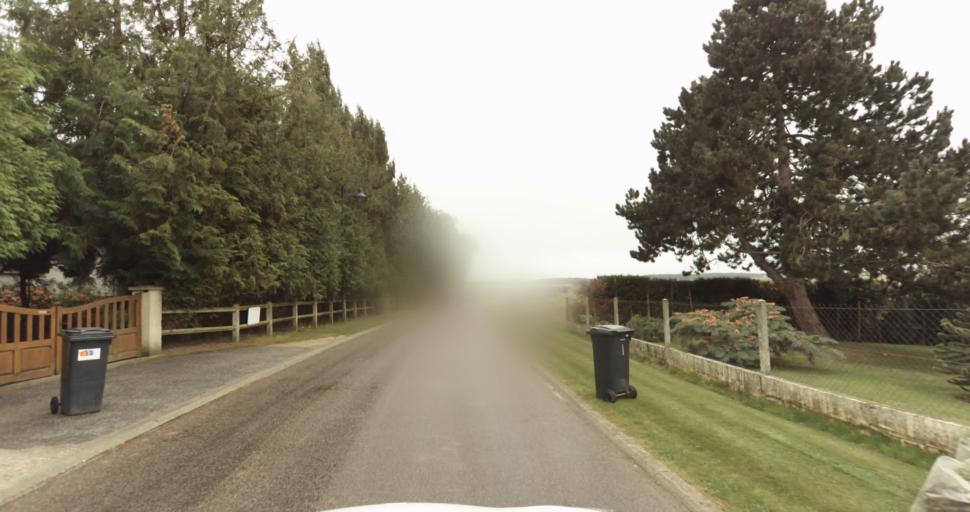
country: FR
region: Haute-Normandie
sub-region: Departement de l'Eure
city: Normanville
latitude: 49.0817
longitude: 1.2029
